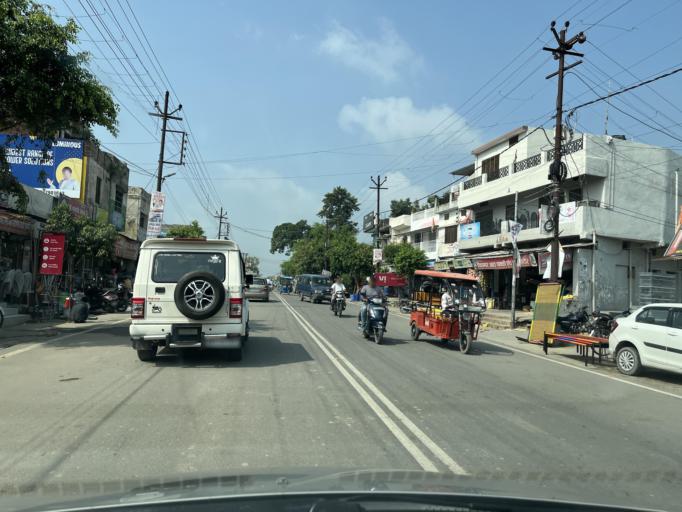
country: IN
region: Uttarakhand
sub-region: Udham Singh Nagar
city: Bazpur
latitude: 29.1628
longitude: 79.1561
